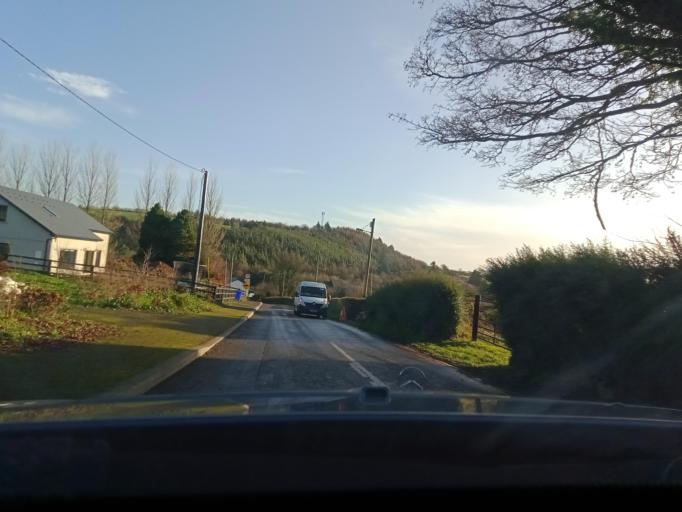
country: IE
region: Leinster
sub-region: Kilkenny
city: Callan
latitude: 52.4613
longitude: -7.3983
